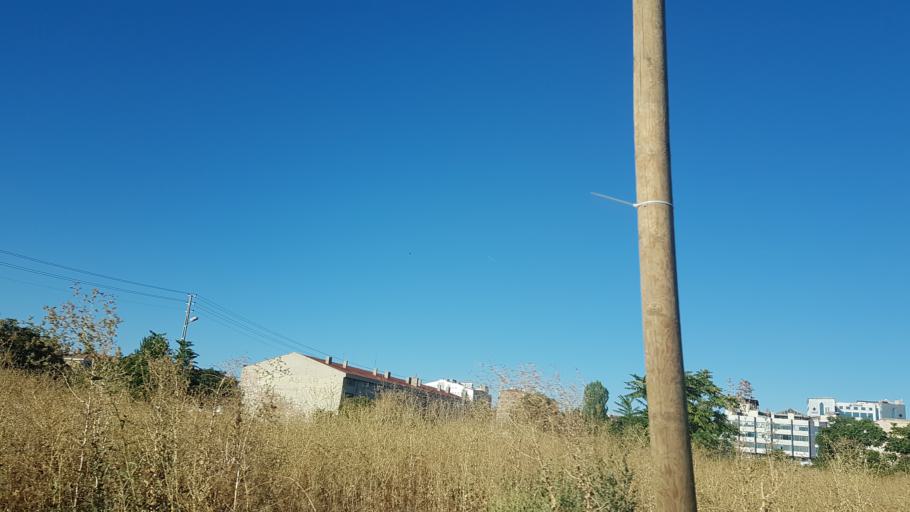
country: TR
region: Ankara
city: Ankara
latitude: 39.9519
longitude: 32.8509
